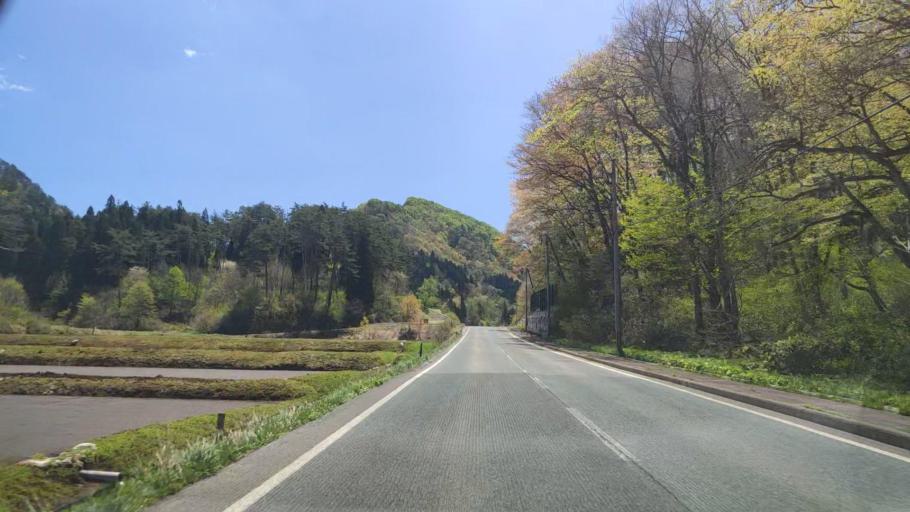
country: JP
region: Yamagata
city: Shinjo
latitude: 38.9023
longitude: 140.3276
